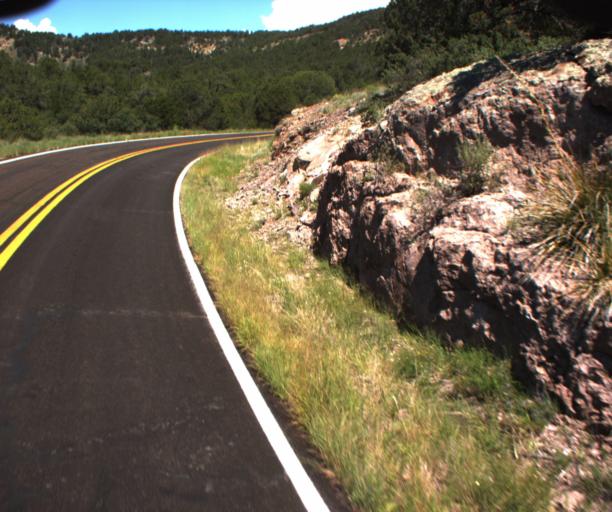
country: US
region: Arizona
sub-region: Greenlee County
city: Morenci
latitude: 33.3870
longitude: -109.3321
